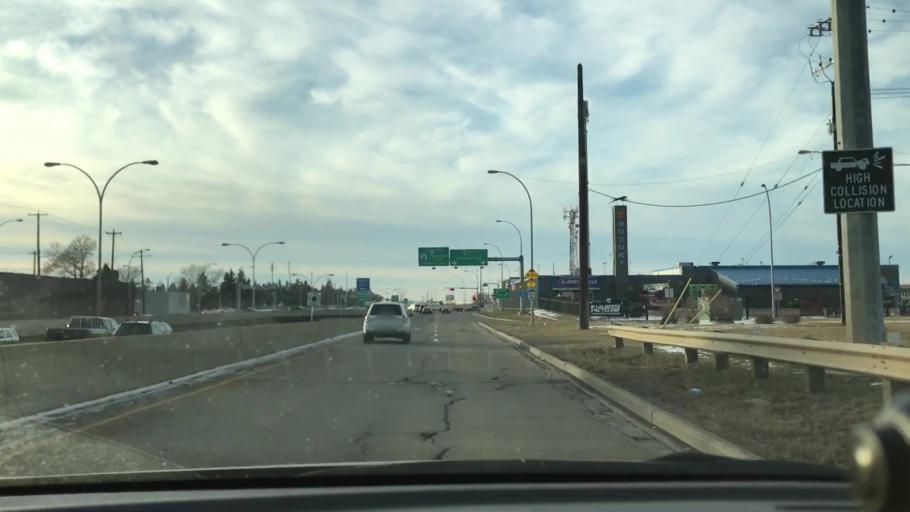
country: CA
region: Alberta
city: Edmonton
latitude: 53.5816
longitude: -113.4888
